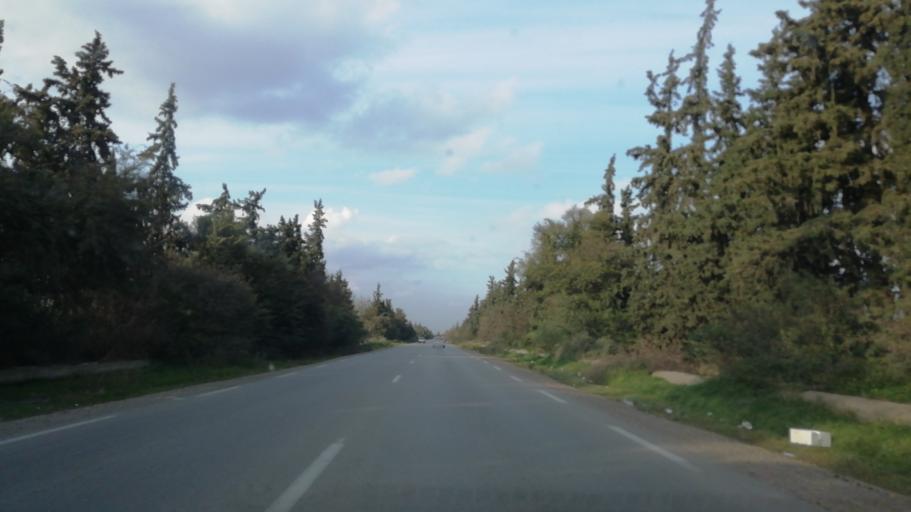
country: DZ
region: Mascara
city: Mascara
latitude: 35.6064
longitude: 0.0524
